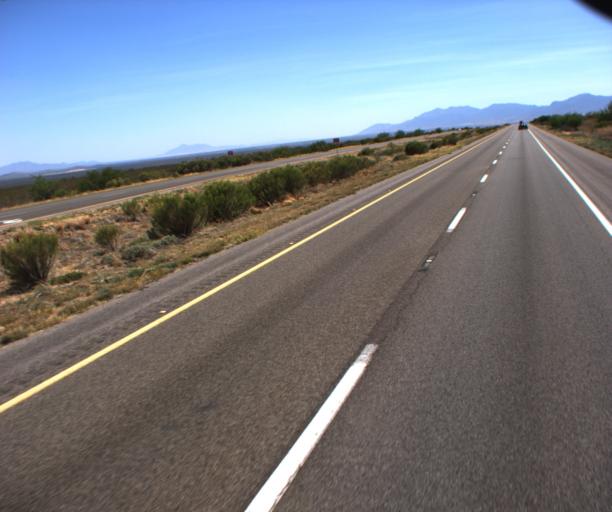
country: US
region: Arizona
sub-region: Cochise County
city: Huachuca City
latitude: 31.7808
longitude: -110.3503
